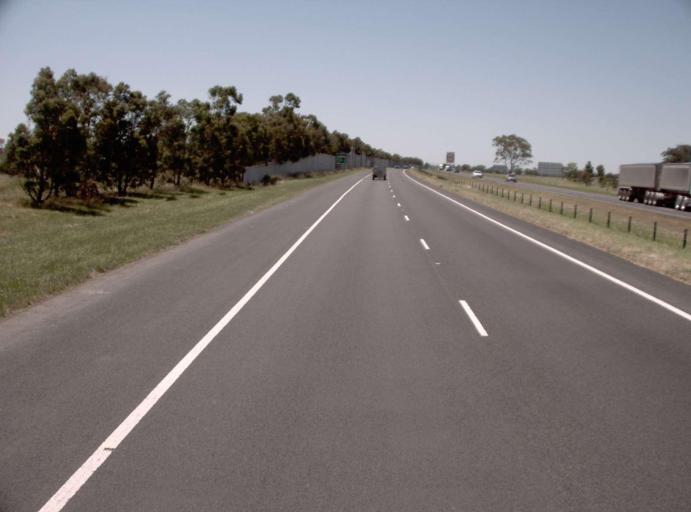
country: AU
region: Victoria
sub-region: Cardinia
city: Officer
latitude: -38.0817
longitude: 145.4420
